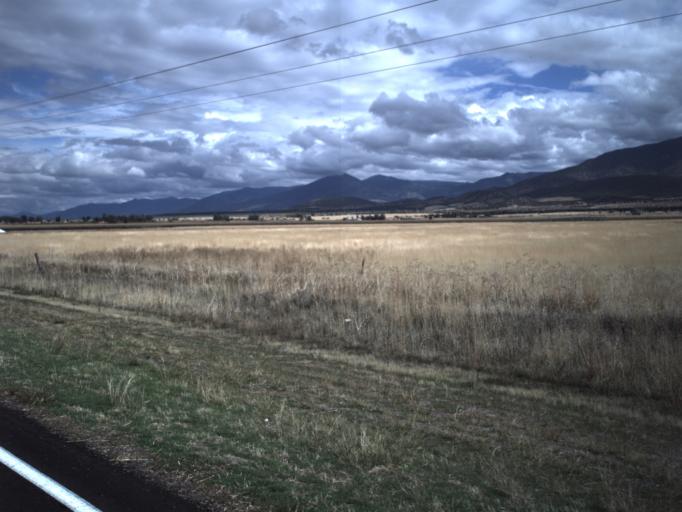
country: US
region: Utah
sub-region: Millard County
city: Fillmore
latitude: 38.8656
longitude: -112.4170
